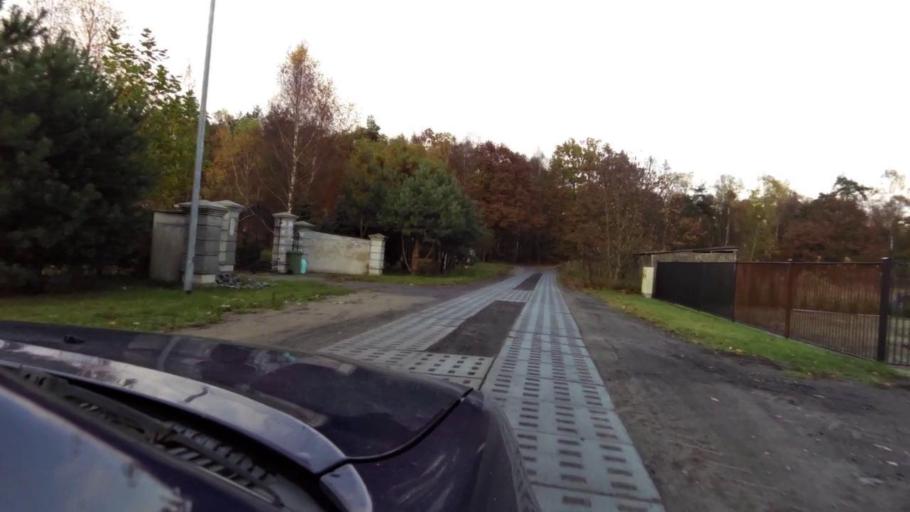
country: PL
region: West Pomeranian Voivodeship
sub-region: Powiat goleniowski
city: Goleniow
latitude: 53.5786
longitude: 14.7649
